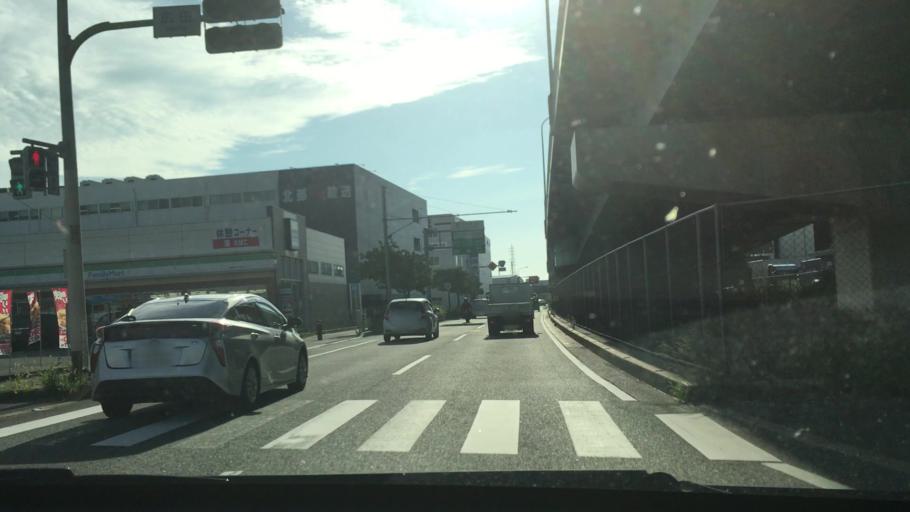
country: JP
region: Fukuoka
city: Fukuoka-shi
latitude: 33.6257
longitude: 130.4603
